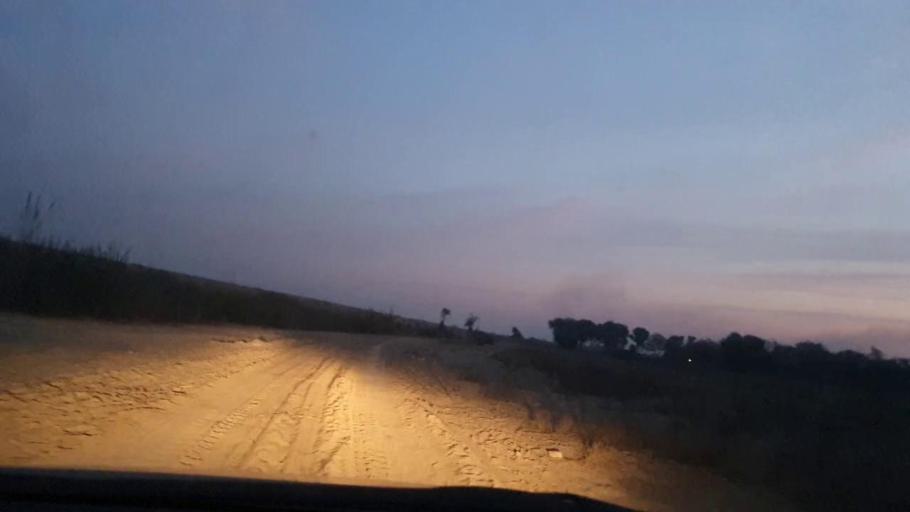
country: PK
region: Sindh
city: Sakrand
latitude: 26.1827
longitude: 68.3077
